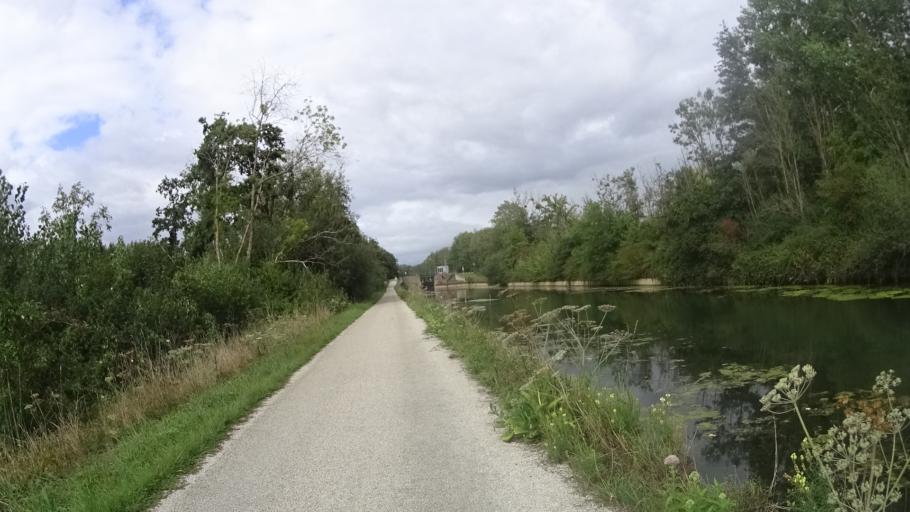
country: FR
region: Picardie
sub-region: Departement de l'Aisne
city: Itancourt
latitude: 49.7676
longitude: 3.3883
